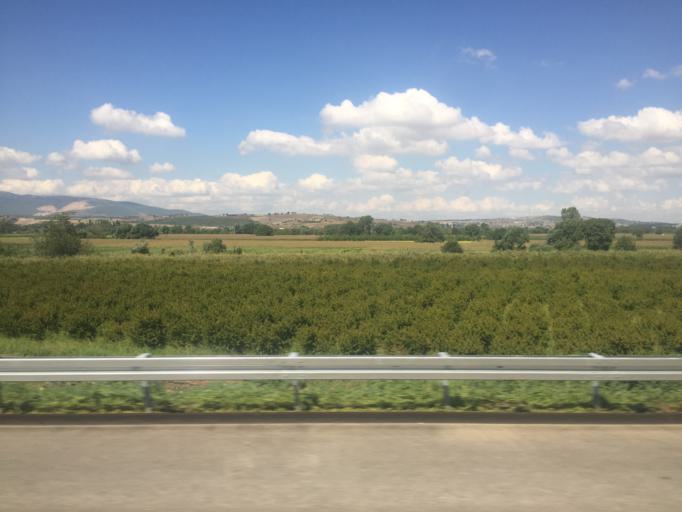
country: TR
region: Balikesir
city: Gobel
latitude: 39.9992
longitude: 28.1926
